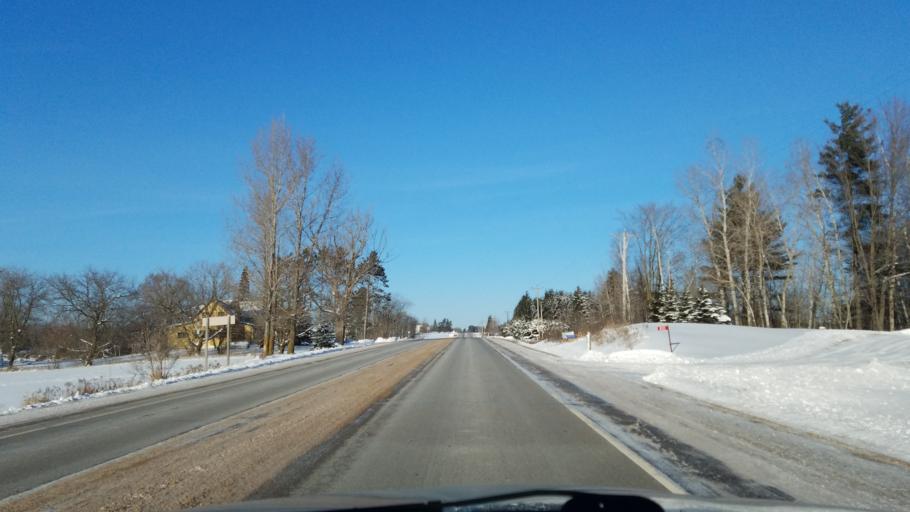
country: US
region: Wisconsin
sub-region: Barron County
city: Cumberland
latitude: 45.5112
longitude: -92.0522
